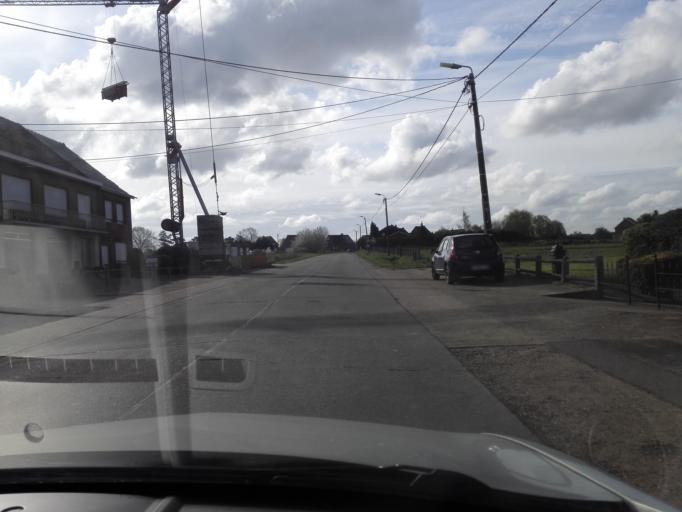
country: BE
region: Flanders
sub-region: Provincie Vlaams-Brabant
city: Aarschot
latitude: 50.9553
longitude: 4.8987
